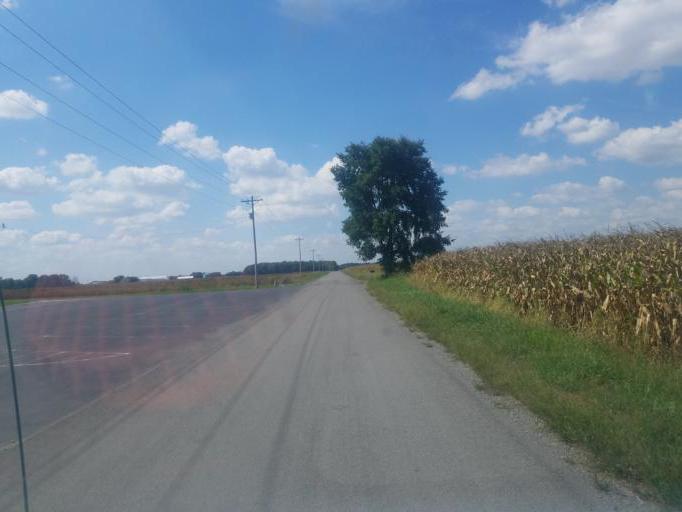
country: US
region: Ohio
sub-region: Hardin County
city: Ada
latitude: 40.6601
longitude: -83.8414
